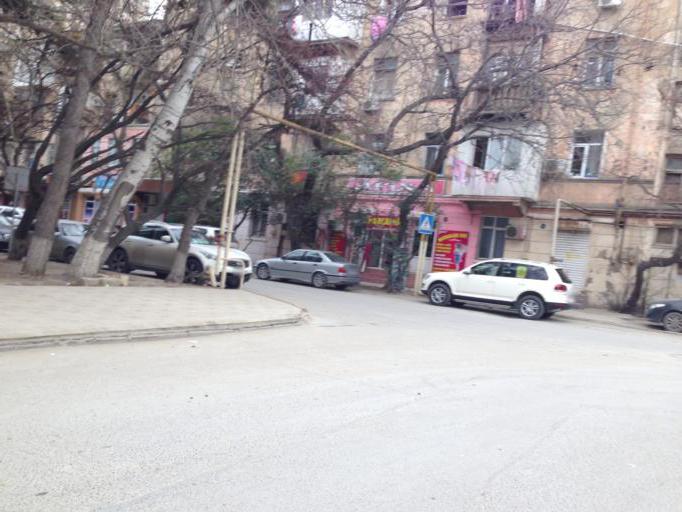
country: AZ
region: Baki
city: Baku
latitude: 40.4000
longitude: 49.8708
